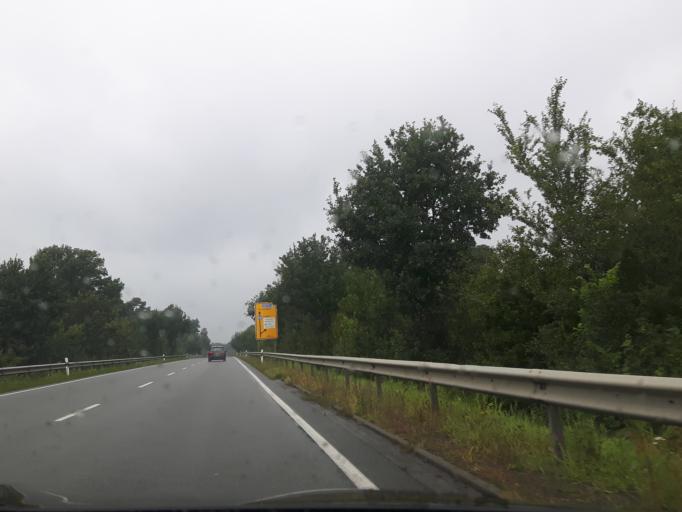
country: DE
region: Lower Saxony
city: Lingen
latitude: 52.4976
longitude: 7.2854
